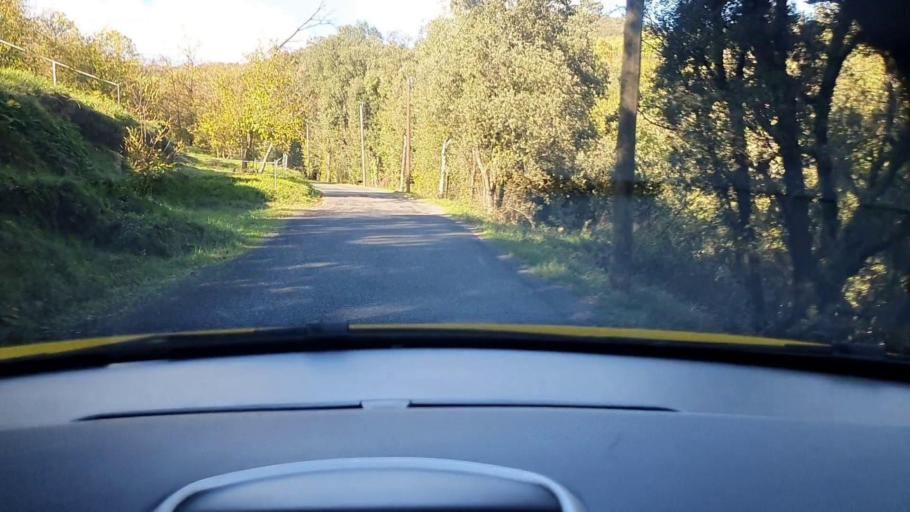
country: FR
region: Languedoc-Roussillon
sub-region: Departement du Gard
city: Le Vigan
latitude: 43.9964
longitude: 3.6278
